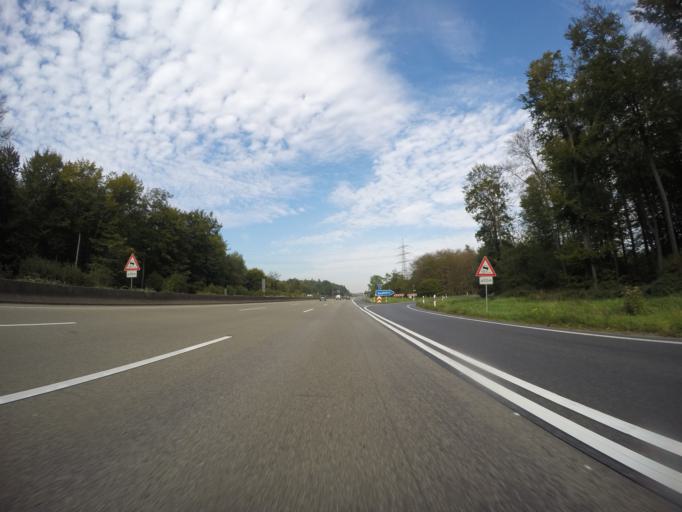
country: DE
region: Hesse
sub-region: Regierungsbezirk Darmstadt
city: Seligenstadt
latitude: 50.0328
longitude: 8.9382
